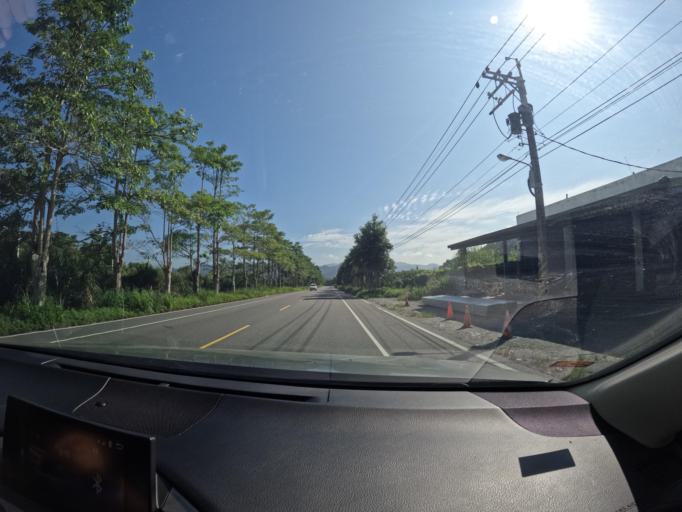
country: TW
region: Taiwan
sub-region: Hualien
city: Hualian
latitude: 23.4830
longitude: 121.3693
